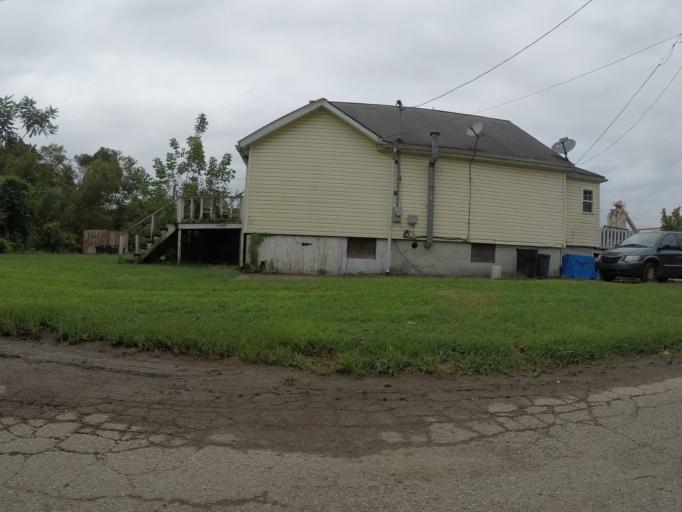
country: US
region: West Virginia
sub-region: Cabell County
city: Pea Ridge
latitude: 38.4300
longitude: -82.3721
